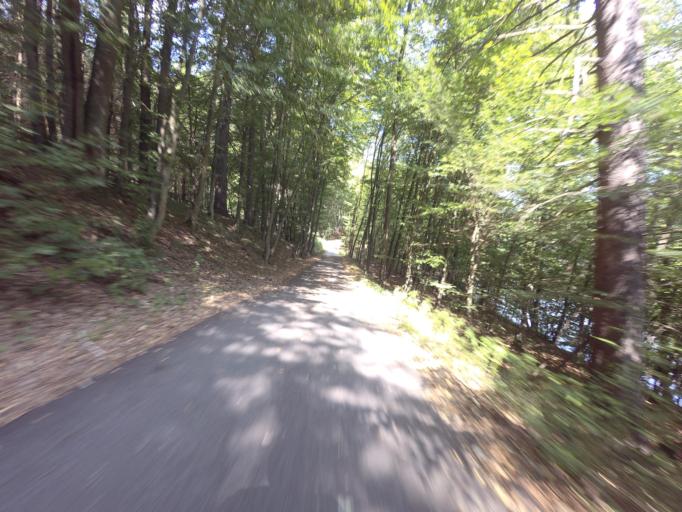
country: CZ
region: Jihocesky
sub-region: Okres Ceske Budejovice
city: Hluboka nad Vltavou
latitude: 49.0824
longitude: 14.4593
